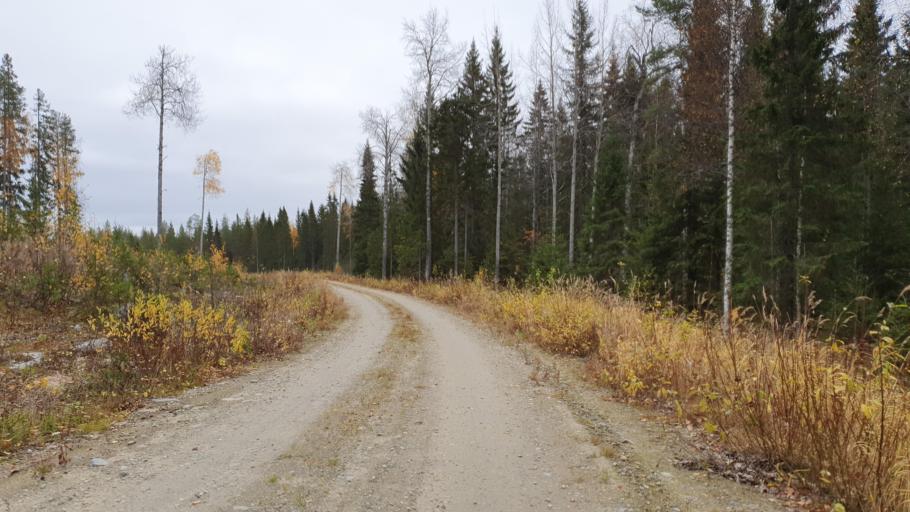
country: FI
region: Kainuu
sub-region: Kehys-Kainuu
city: Kuhmo
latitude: 64.4443
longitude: 29.6435
